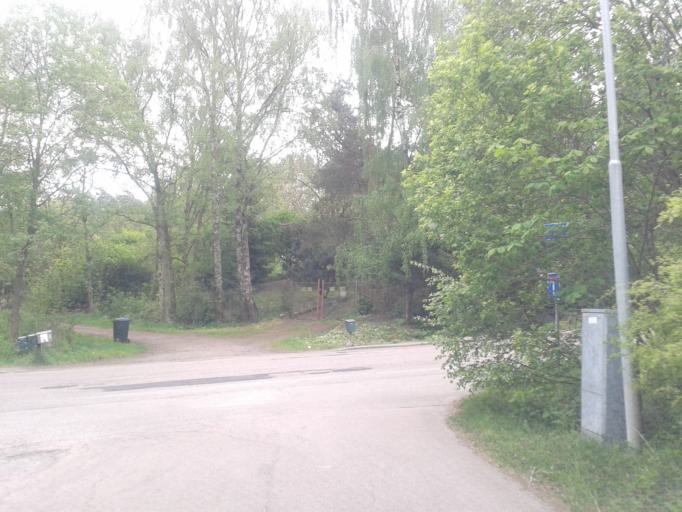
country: SE
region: Vaestra Goetaland
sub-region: Kungalvs Kommun
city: Kungalv
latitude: 57.8550
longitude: 11.9970
